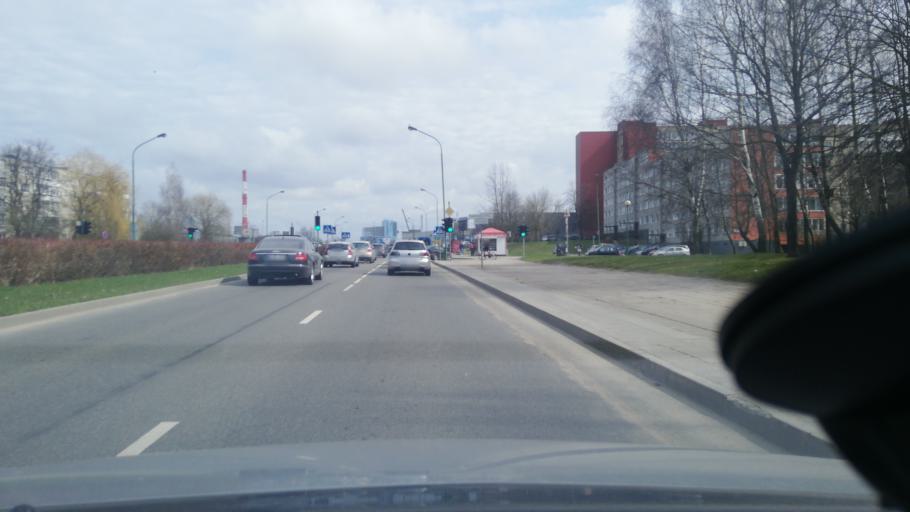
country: LT
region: Klaipedos apskritis
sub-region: Klaipeda
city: Klaipeda
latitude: 55.6761
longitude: 21.1851
